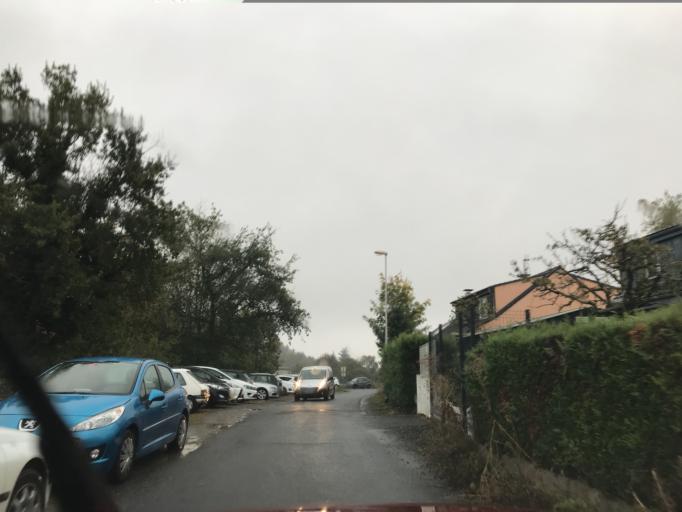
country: FR
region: Auvergne
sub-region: Departement du Puy-de-Dome
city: Durtol
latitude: 45.7992
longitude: 3.0545
